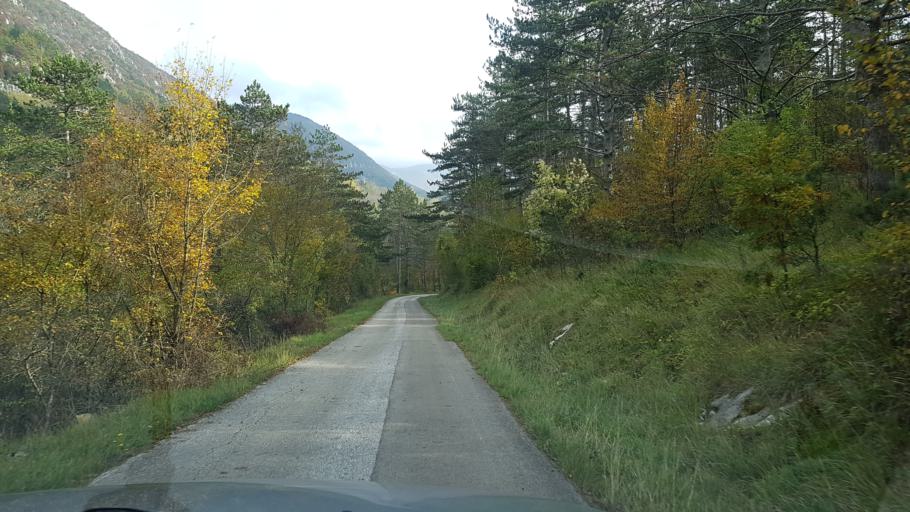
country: HR
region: Istarska
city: Buzet
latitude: 45.4277
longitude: 14.0700
